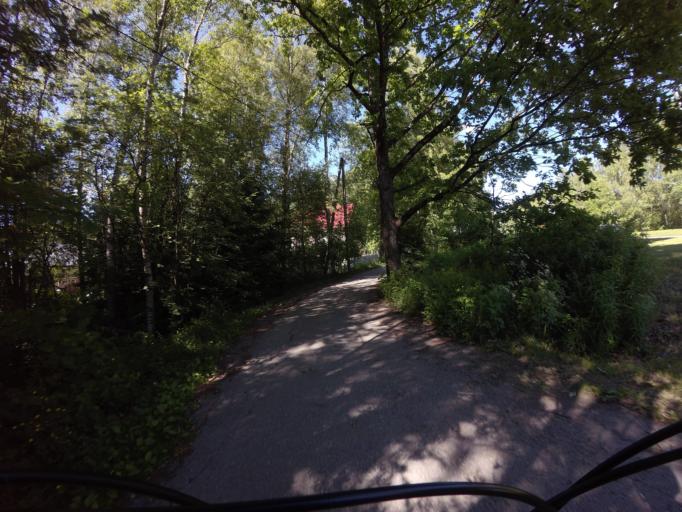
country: FI
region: Varsinais-Suomi
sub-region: Turku
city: Turku
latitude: 60.4870
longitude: 22.2763
